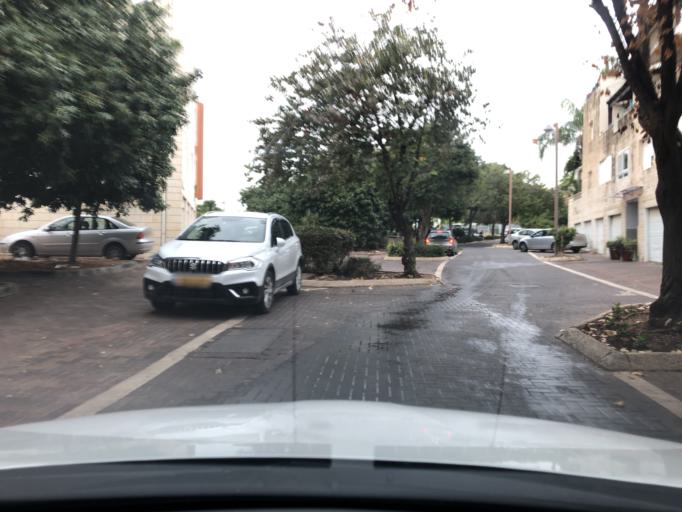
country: IL
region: Central District
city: Modiin
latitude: 31.9066
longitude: 35.0098
